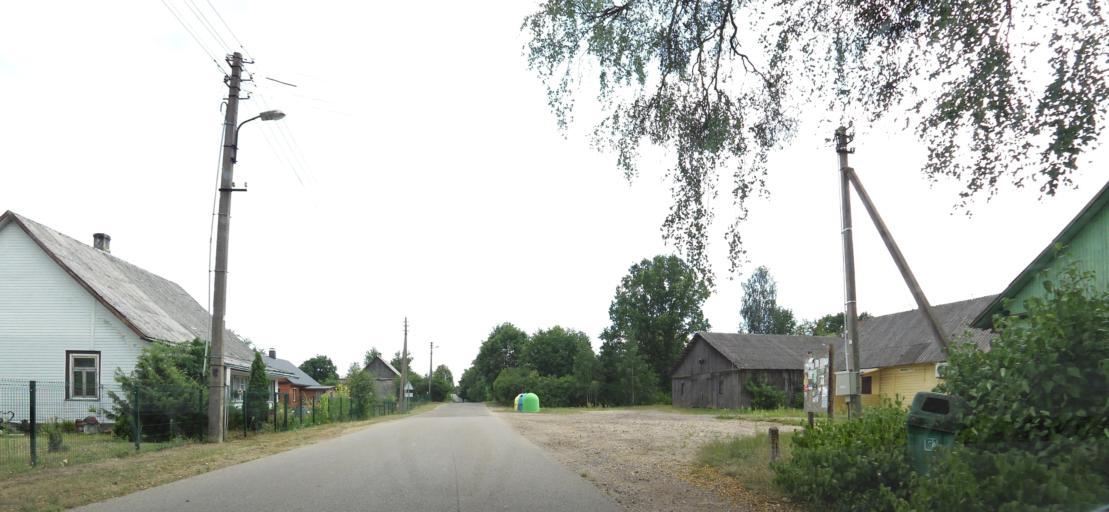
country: LT
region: Alytaus apskritis
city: Varena
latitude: 54.0565
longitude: 24.4043
